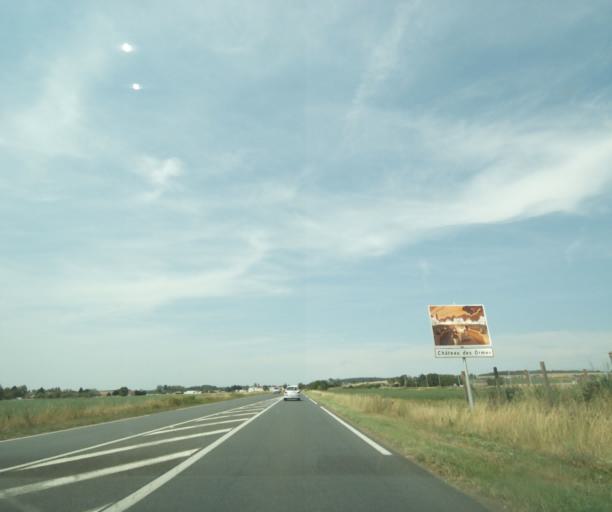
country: FR
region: Poitou-Charentes
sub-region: Departement de la Vienne
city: Dange-Saint-Romain
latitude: 46.9530
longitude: 0.6075
